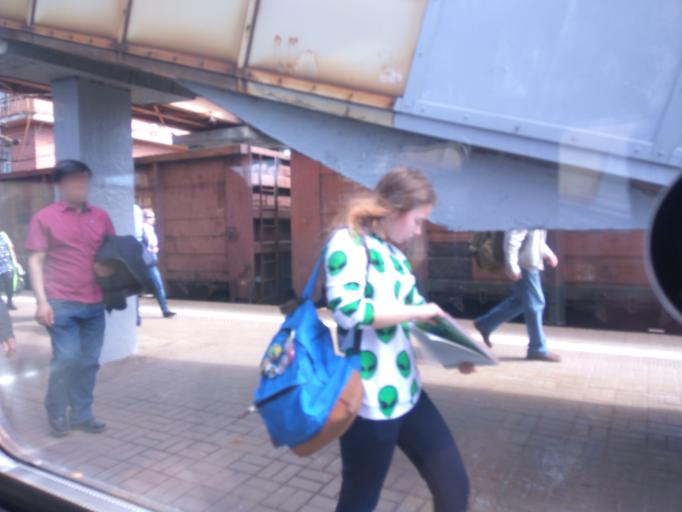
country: RU
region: Moskovskaya
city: Lobnya
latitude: 56.0132
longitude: 37.4852
